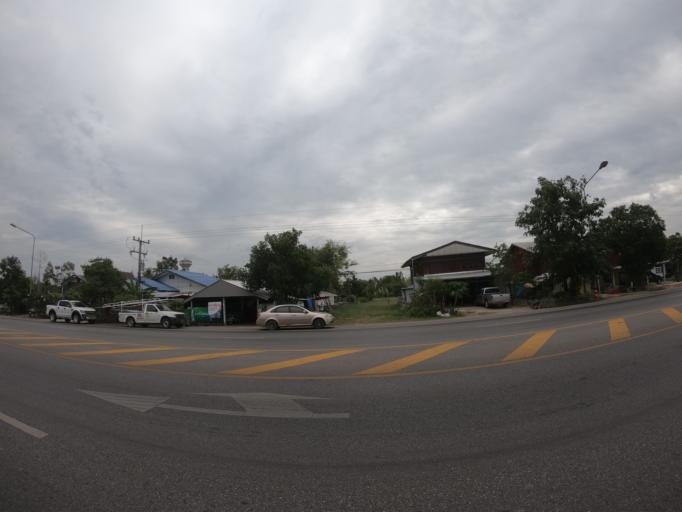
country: TH
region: Roi Et
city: Thawat Buri
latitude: 16.0828
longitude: 103.7245
